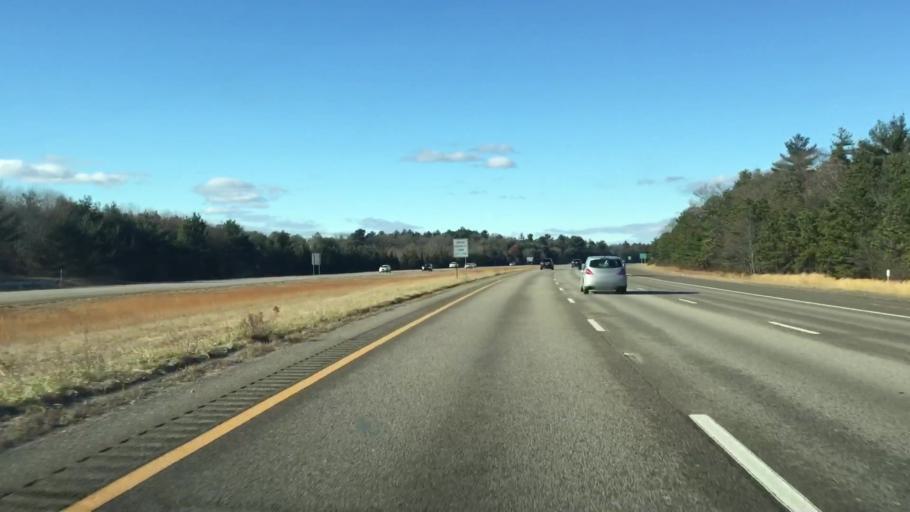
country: US
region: Massachusetts
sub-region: Bristol County
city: Norton Center
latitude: 41.9654
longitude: -71.1379
